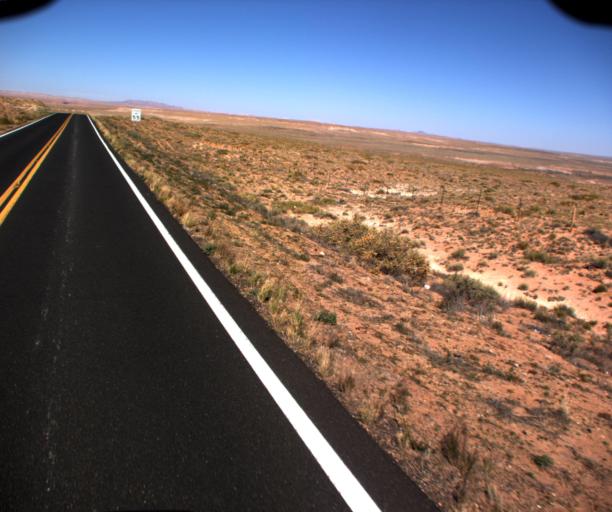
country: US
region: Arizona
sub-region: Coconino County
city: Tuba City
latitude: 36.0807
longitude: -111.1861
